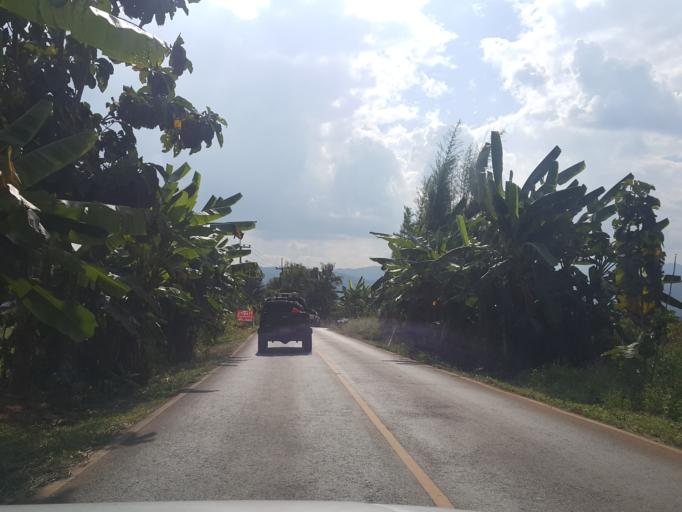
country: TH
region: Chiang Mai
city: Mae Chaem
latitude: 18.4986
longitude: 98.3926
